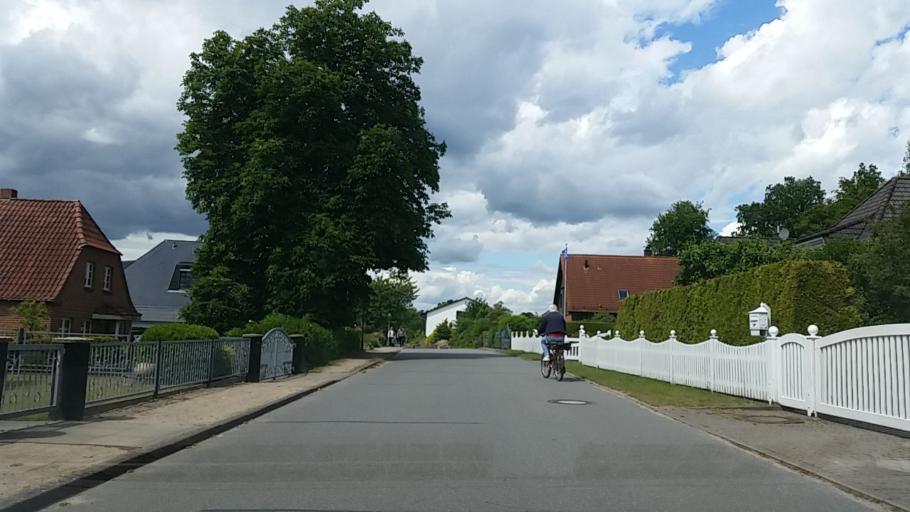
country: DE
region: Schleswig-Holstein
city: Dahmker
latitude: 53.6043
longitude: 10.4515
